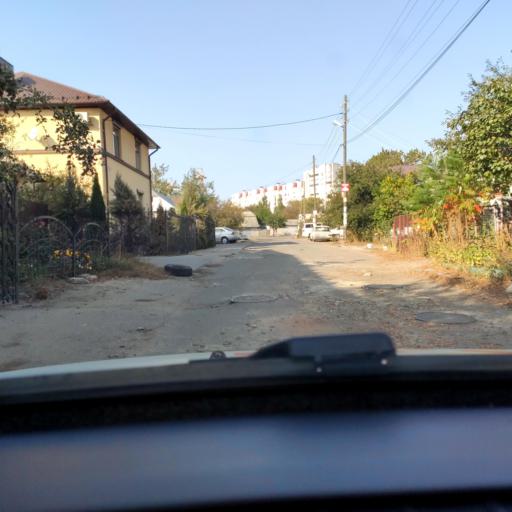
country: RU
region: Voronezj
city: Voronezh
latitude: 51.6921
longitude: 39.2024
